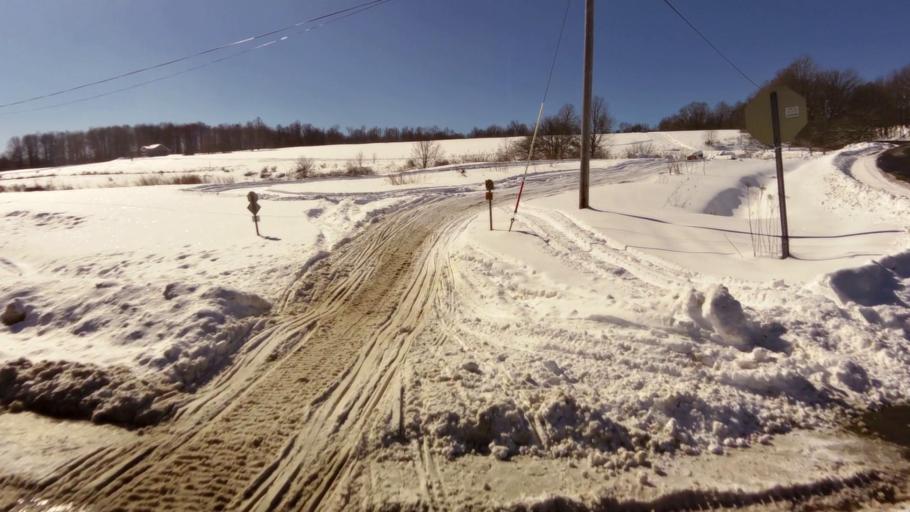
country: US
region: New York
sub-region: Chautauqua County
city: Celoron
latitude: 42.2304
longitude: -79.2992
